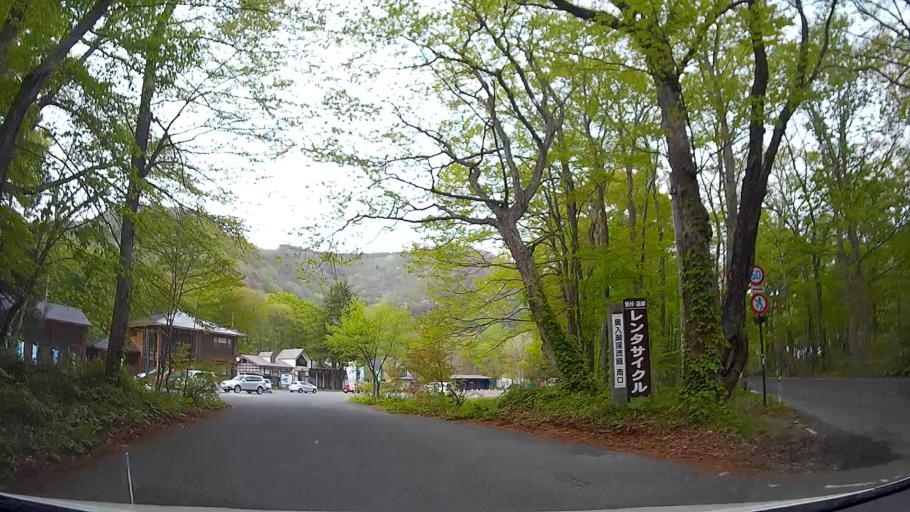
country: JP
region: Aomori
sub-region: Aomori Shi
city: Furudate
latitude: 40.5743
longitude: 140.9789
